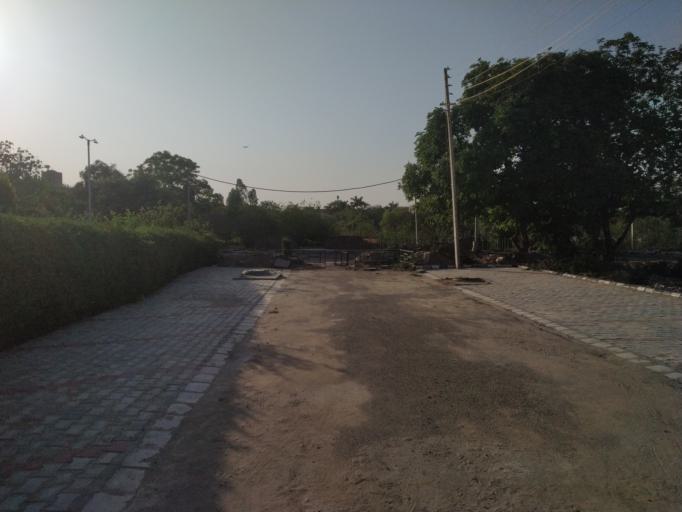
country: IN
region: Punjab
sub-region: Ajitgarh
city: Mohali
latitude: 30.6862
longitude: 76.7479
